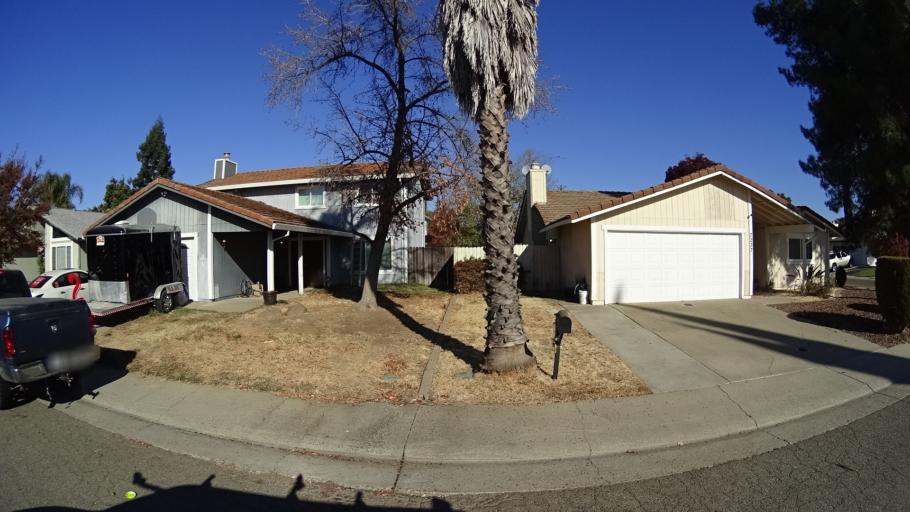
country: US
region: California
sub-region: Sacramento County
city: Citrus Heights
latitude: 38.7206
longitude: -121.2993
